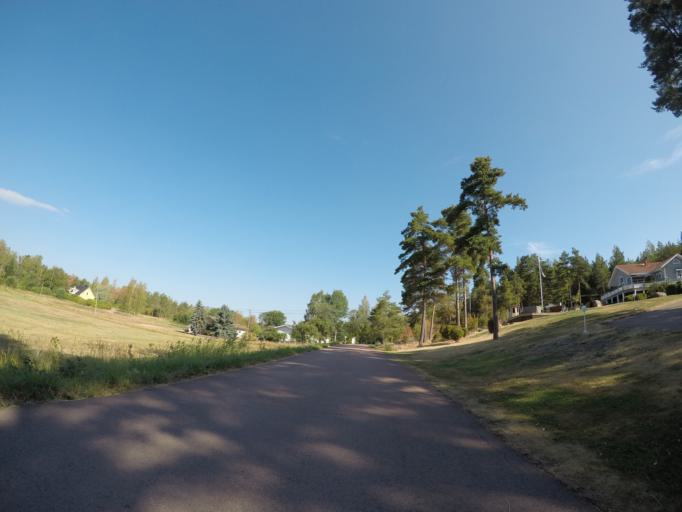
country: AX
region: Alands landsbygd
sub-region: Finstroem
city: Finstroem
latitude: 60.3329
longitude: 19.9111
